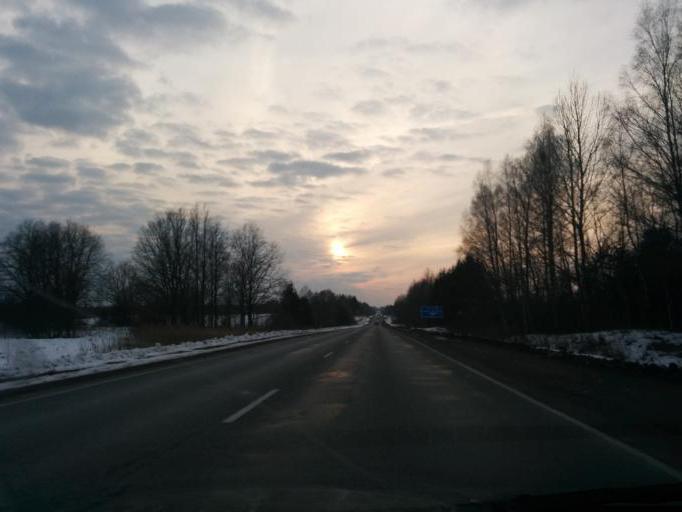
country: LV
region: Raunas
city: Rauna
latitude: 57.3101
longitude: 25.6379
